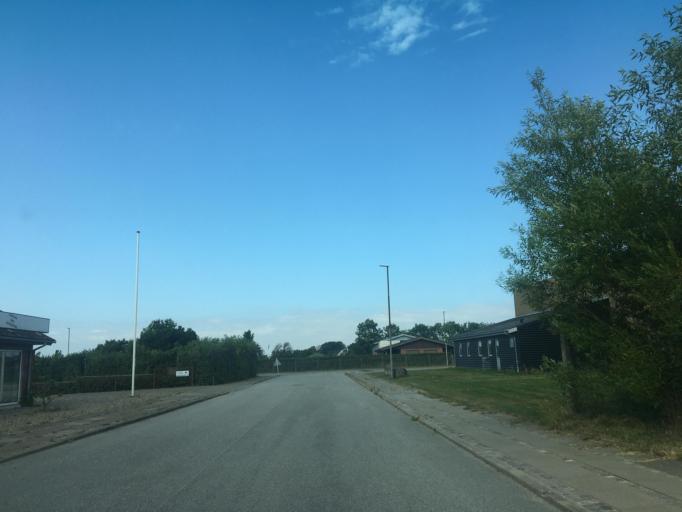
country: DK
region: North Denmark
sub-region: Thisted Kommune
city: Hurup
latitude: 56.7503
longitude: 8.4292
